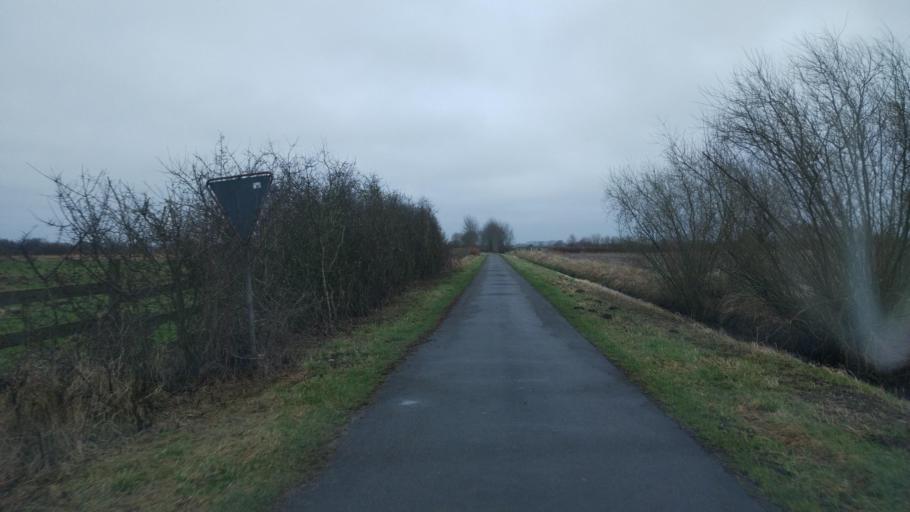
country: DE
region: Schleswig-Holstein
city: Hollingstedt
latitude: 54.4788
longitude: 9.3441
